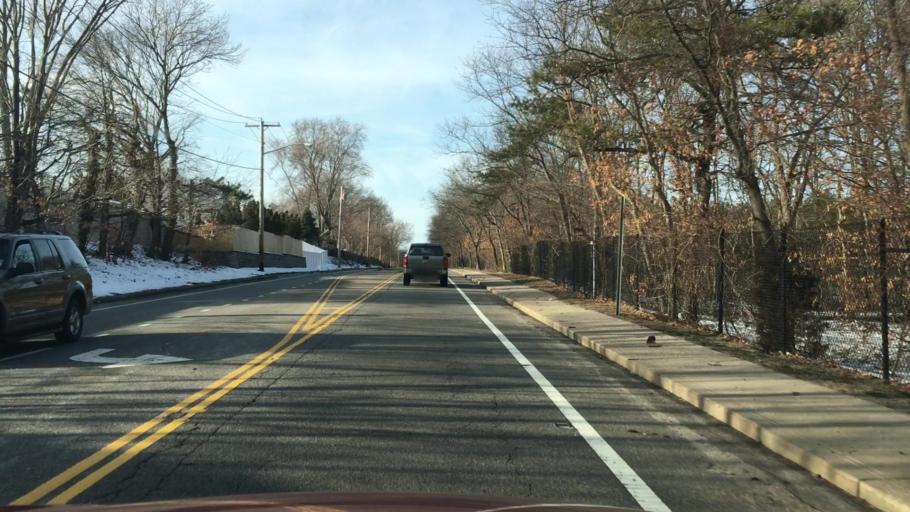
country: US
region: New York
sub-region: Suffolk County
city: Terryville
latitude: 40.8835
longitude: -73.0782
